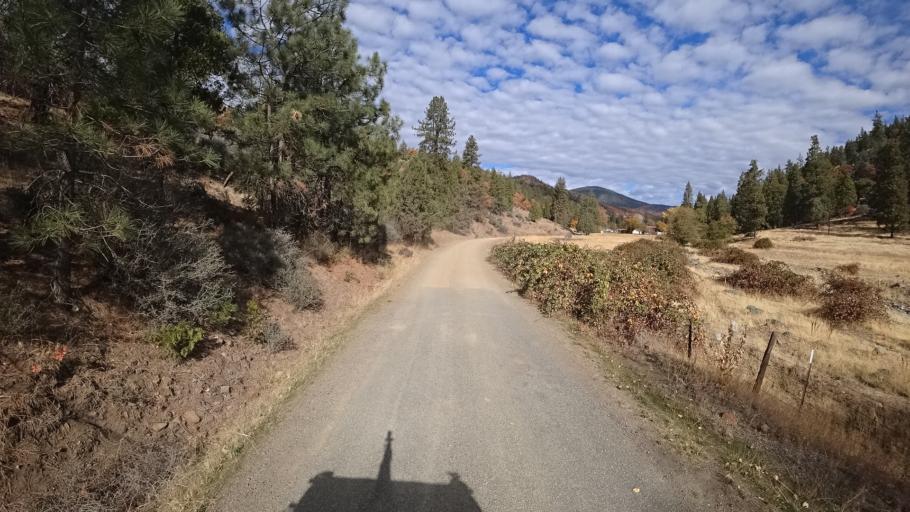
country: US
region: California
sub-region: Siskiyou County
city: Yreka
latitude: 41.6367
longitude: -122.7511
